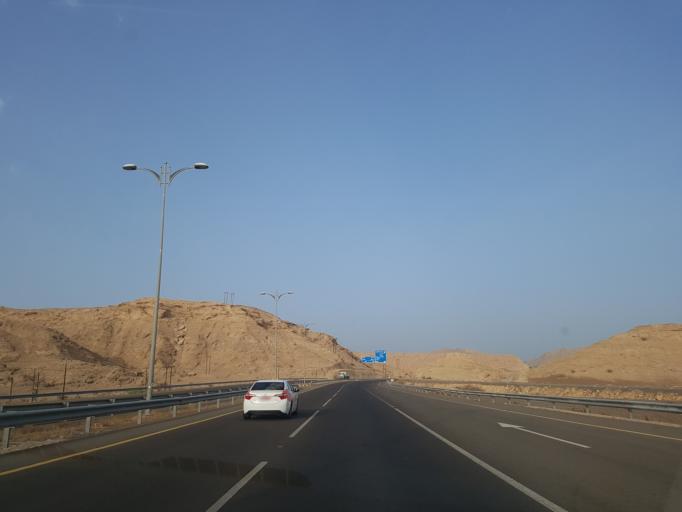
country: OM
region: Al Buraimi
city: Al Buraymi
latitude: 24.2334
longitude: 55.9368
